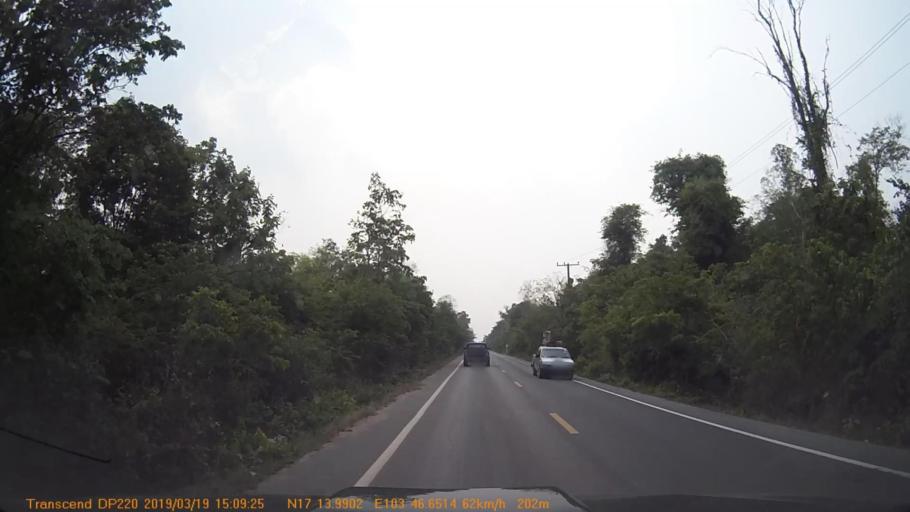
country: TH
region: Sakon Nakhon
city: Nikhom Nam Un
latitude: 17.2332
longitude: 103.7773
